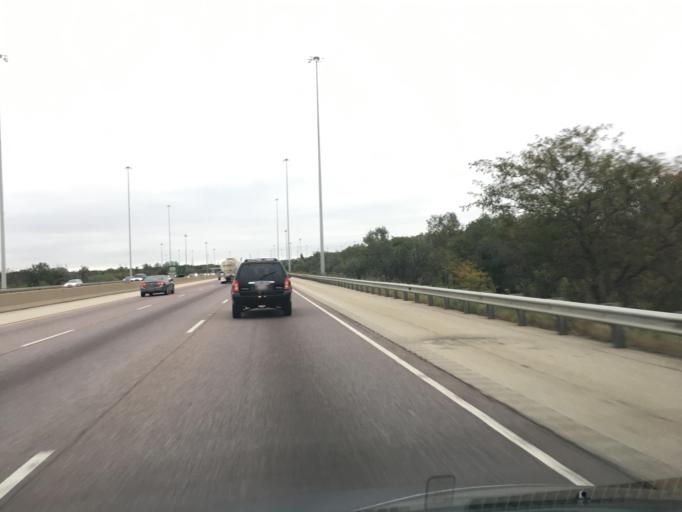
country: US
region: Illinois
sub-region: Cook County
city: Summit
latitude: 41.7863
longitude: -87.8276
